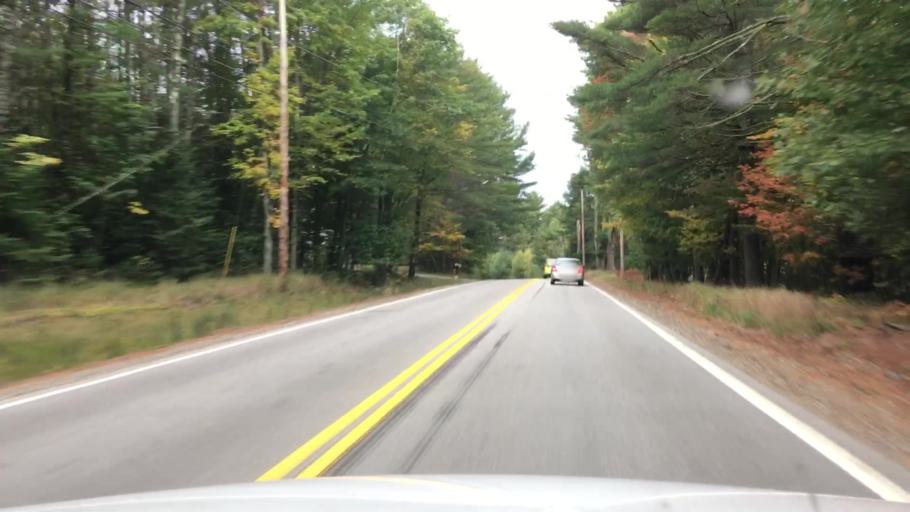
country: US
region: Maine
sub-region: Oxford County
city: Norway
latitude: 44.2242
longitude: -70.6321
